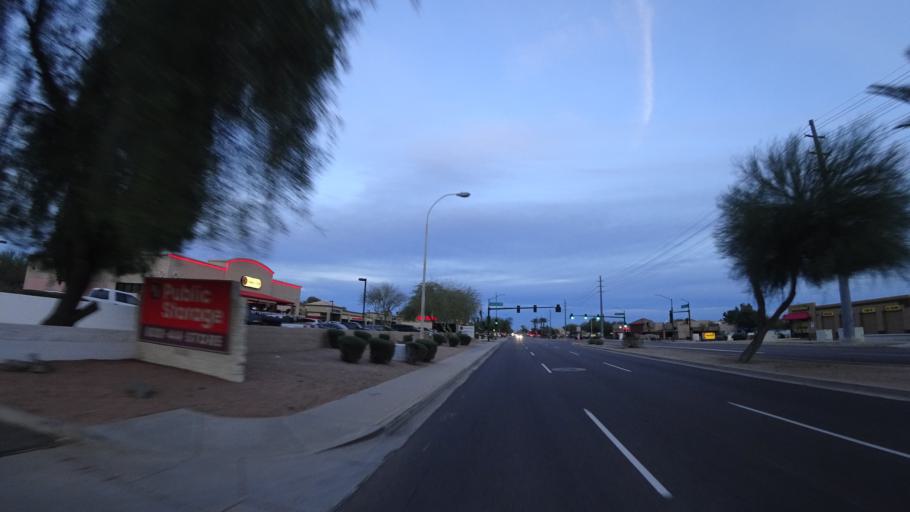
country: US
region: Arizona
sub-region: Maricopa County
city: Guadalupe
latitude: 33.3053
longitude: -111.9936
